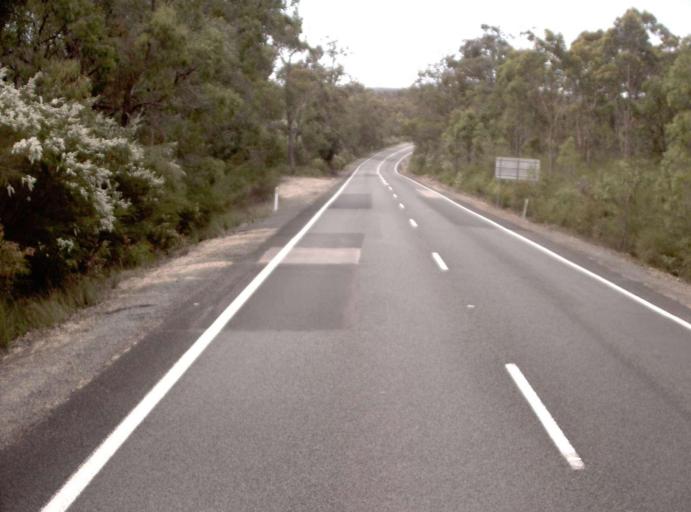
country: AU
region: New South Wales
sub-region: Bega Valley
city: Eden
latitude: -37.4893
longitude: 149.5504
